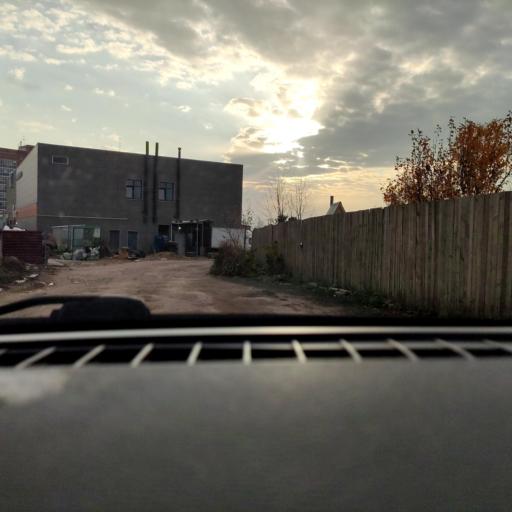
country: RU
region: Perm
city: Froly
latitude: 57.9240
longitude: 56.2725
